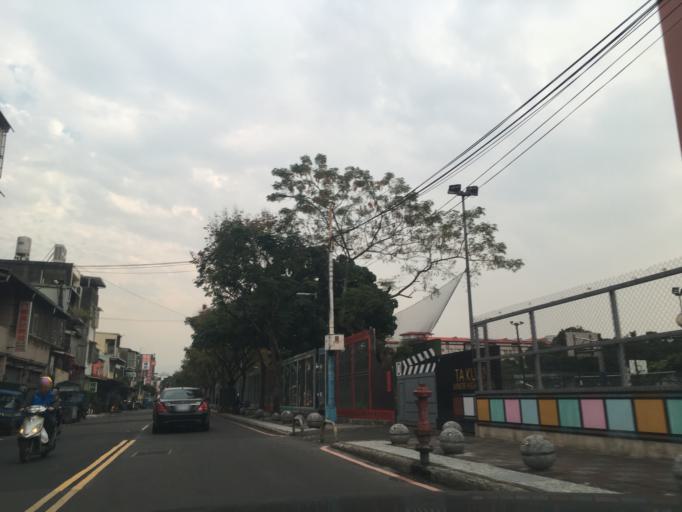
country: TW
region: Taipei
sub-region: Taipei
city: Banqiao
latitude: 25.0109
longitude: 121.4497
